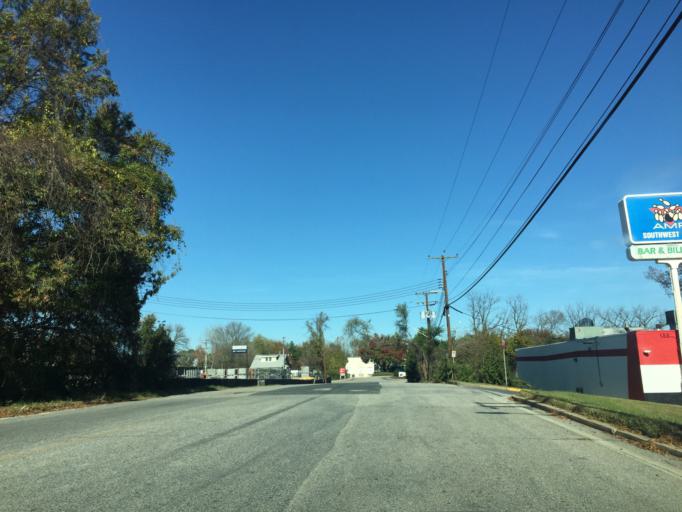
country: US
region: Maryland
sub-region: Baltimore County
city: Lansdowne
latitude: 39.2258
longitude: -76.6605
